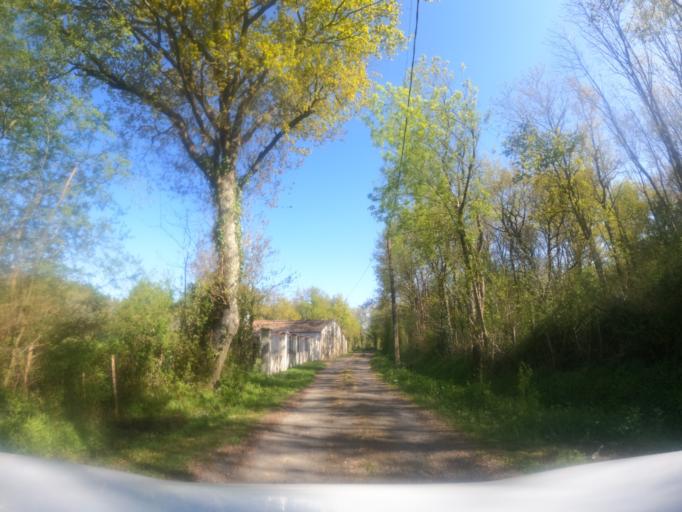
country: FR
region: Pays de la Loire
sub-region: Departement de la Vendee
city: Le Champ-Saint-Pere
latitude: 46.5364
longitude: -1.3462
